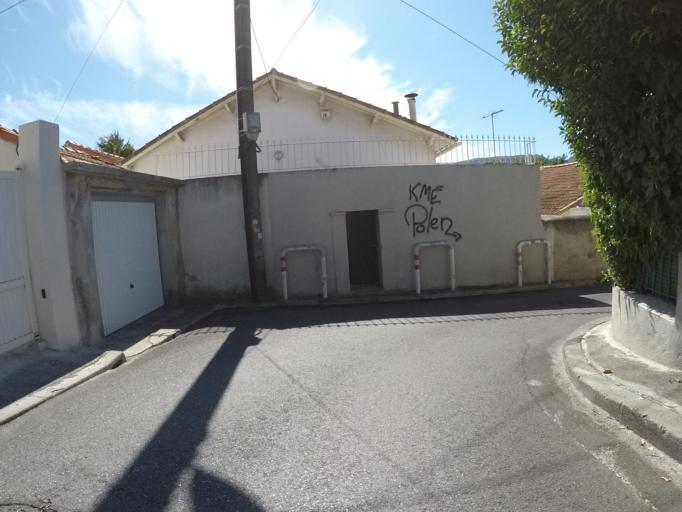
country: FR
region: Provence-Alpes-Cote d'Azur
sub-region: Departement des Bouches-du-Rhone
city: Marseille 09
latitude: 43.2438
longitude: 5.4069
